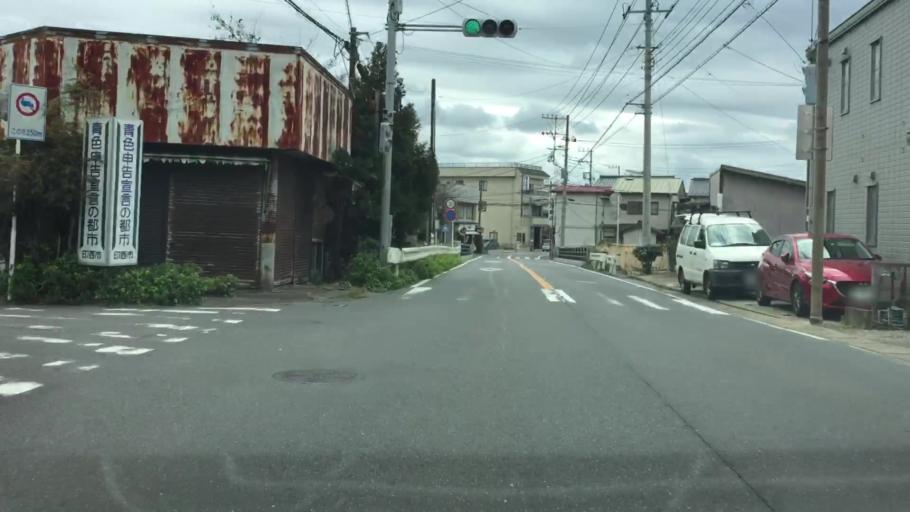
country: JP
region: Ibaraki
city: Ryugasaki
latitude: 35.8433
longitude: 140.1432
